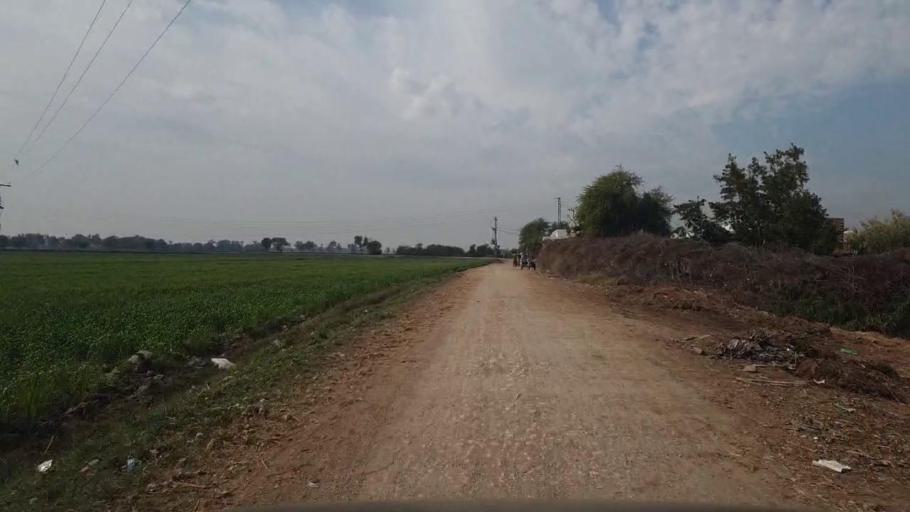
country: PK
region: Sindh
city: Sakrand
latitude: 25.9973
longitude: 68.3821
